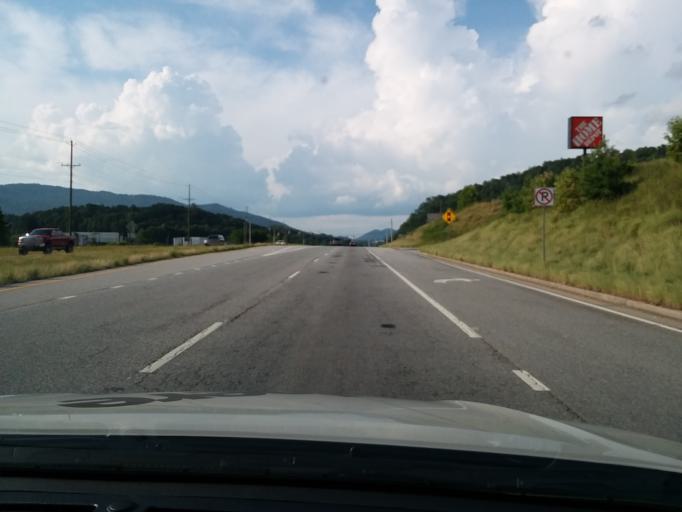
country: US
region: Georgia
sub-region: Rabun County
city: Clayton
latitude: 34.8566
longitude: -83.4074
